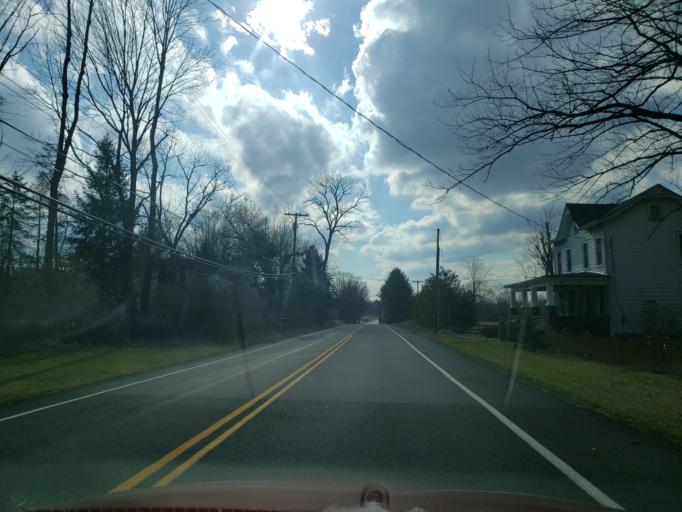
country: US
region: New Jersey
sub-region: Hunterdon County
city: Lambertville
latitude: 40.4413
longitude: -74.9468
